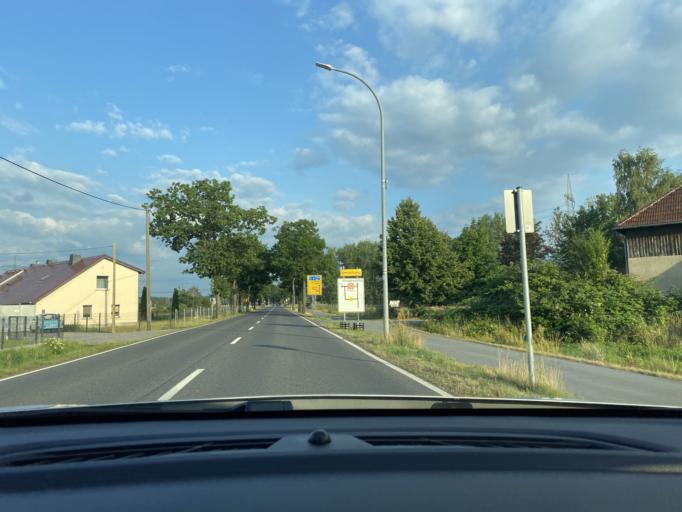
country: DE
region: Saxony
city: Konigswartha
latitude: 51.3491
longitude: 14.3283
